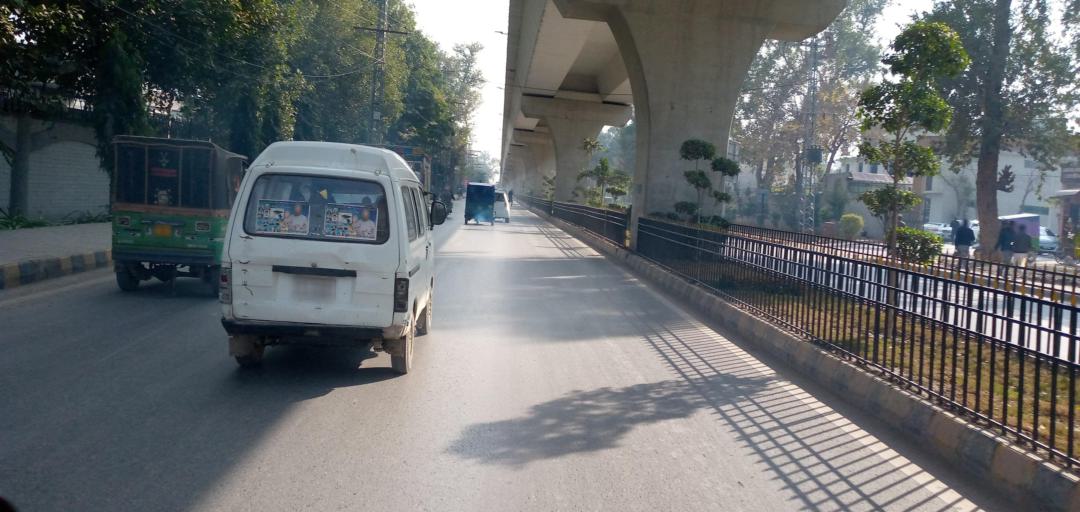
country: PK
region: Khyber Pakhtunkhwa
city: Peshawar
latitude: 34.0023
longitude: 71.5297
